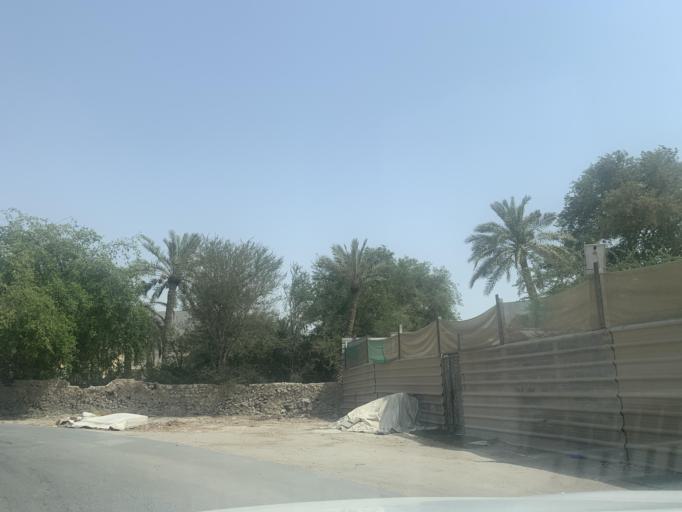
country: BH
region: Manama
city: Jidd Hafs
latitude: 26.2207
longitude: 50.4657
